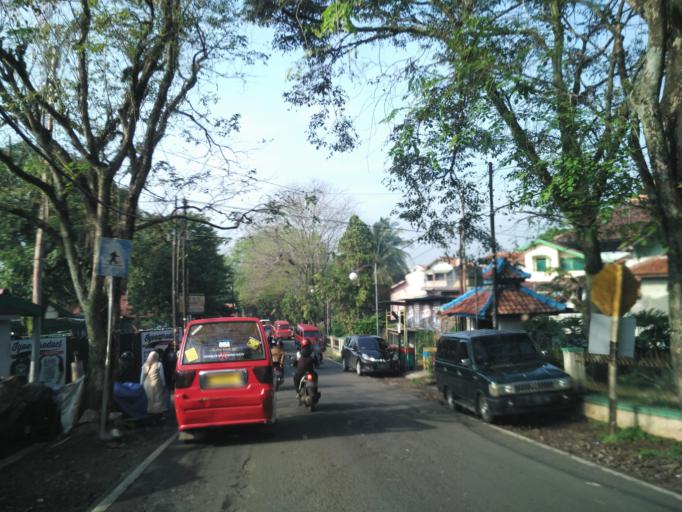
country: ID
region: West Java
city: Ciranjang-hilir
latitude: -6.8267
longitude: 107.1415
